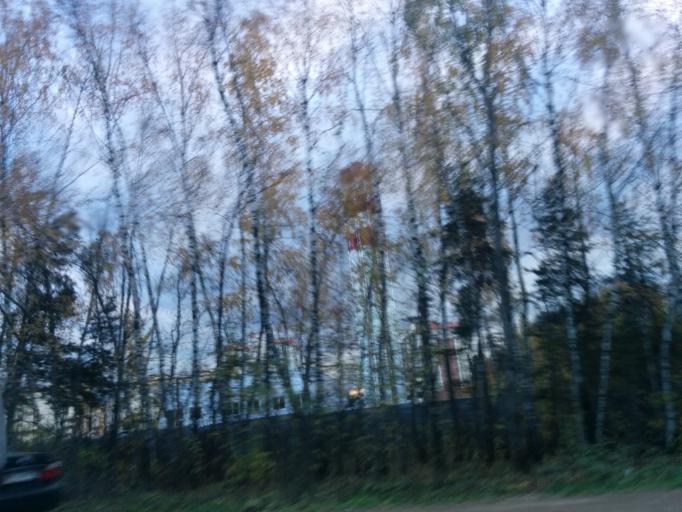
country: RU
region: Moscow
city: Zagor'ye
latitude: 55.5384
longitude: 37.6359
